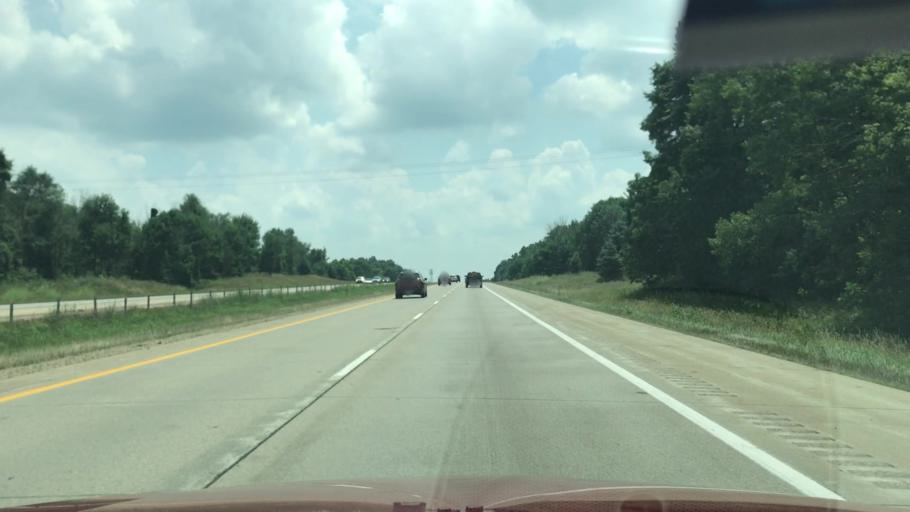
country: US
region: Michigan
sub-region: Allegan County
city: Otsego
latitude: 42.5086
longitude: -85.6547
